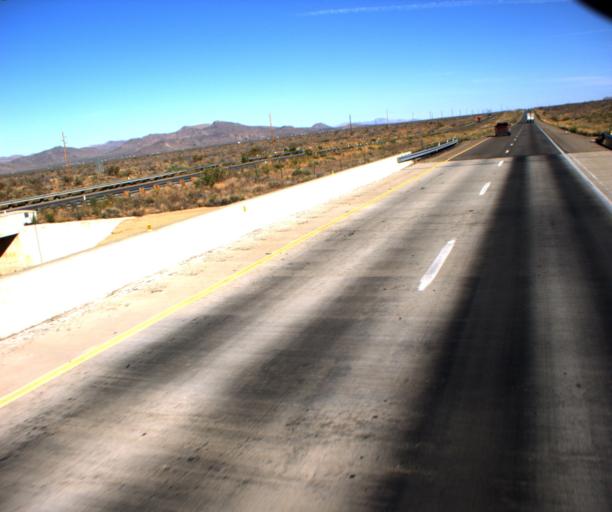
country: US
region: Arizona
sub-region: Mohave County
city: Golden Valley
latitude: 35.3031
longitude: -114.1913
